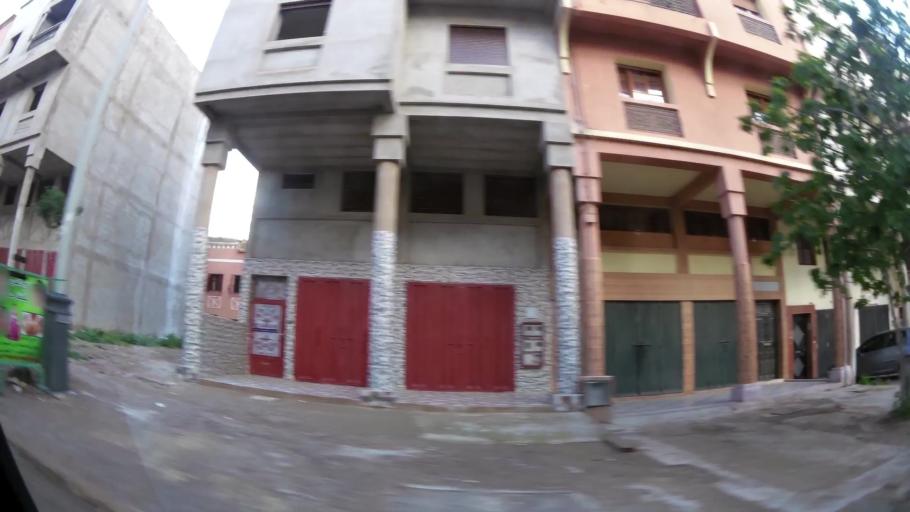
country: MA
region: Chaouia-Ouardigha
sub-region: Settat Province
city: Settat
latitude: 33.0035
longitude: -7.6360
